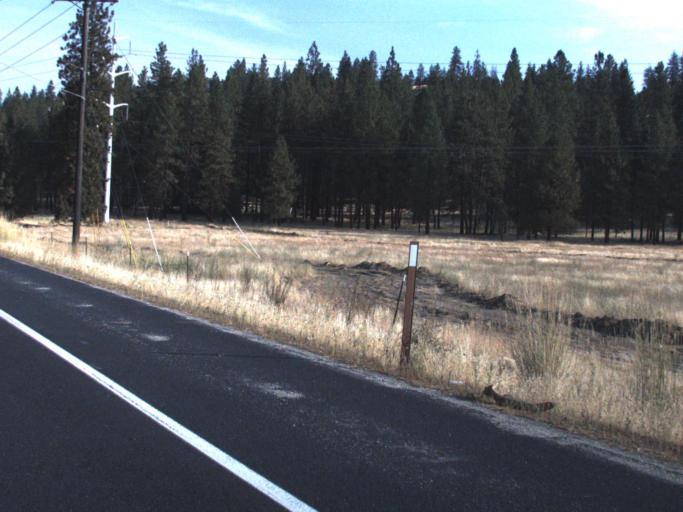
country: US
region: Washington
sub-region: Spokane County
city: Town and Country
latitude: 47.7470
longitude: -117.5075
